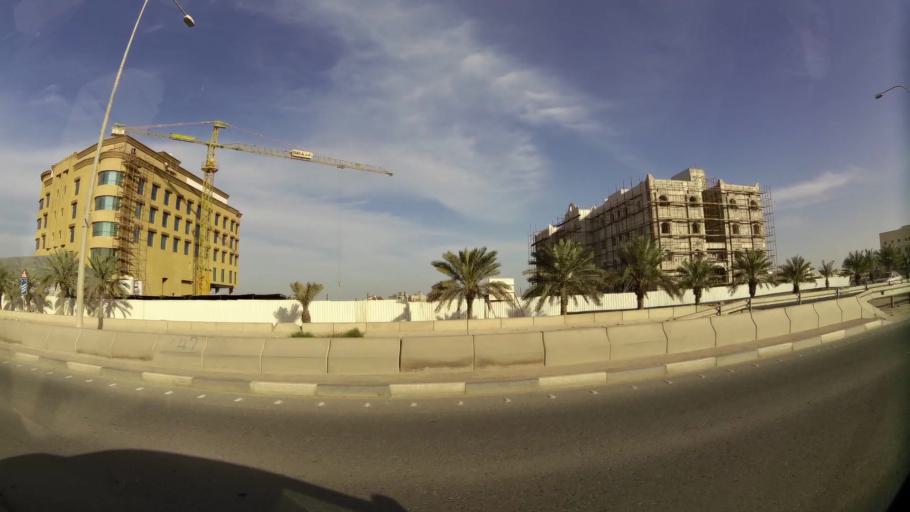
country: QA
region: Al Wakrah
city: Al Wakrah
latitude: 25.1585
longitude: 51.6059
